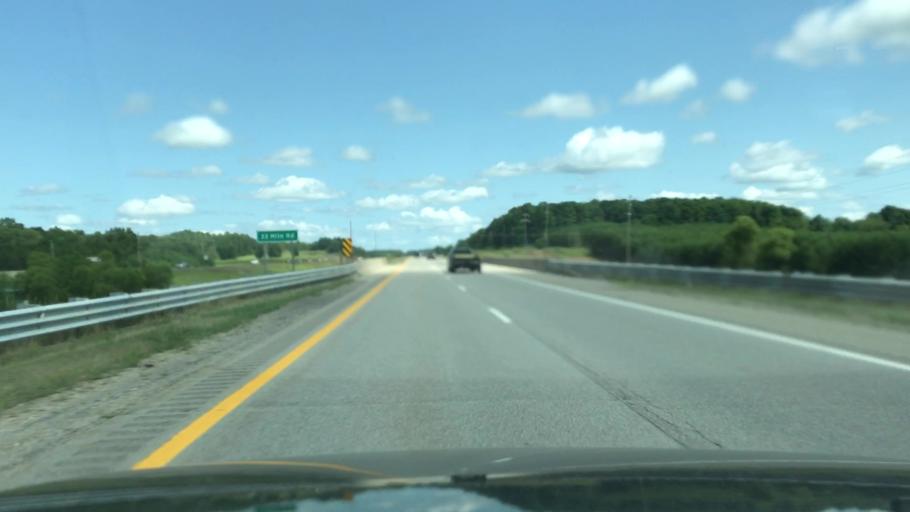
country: US
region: Michigan
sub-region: Osceola County
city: Reed City
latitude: 43.7852
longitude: -85.5337
